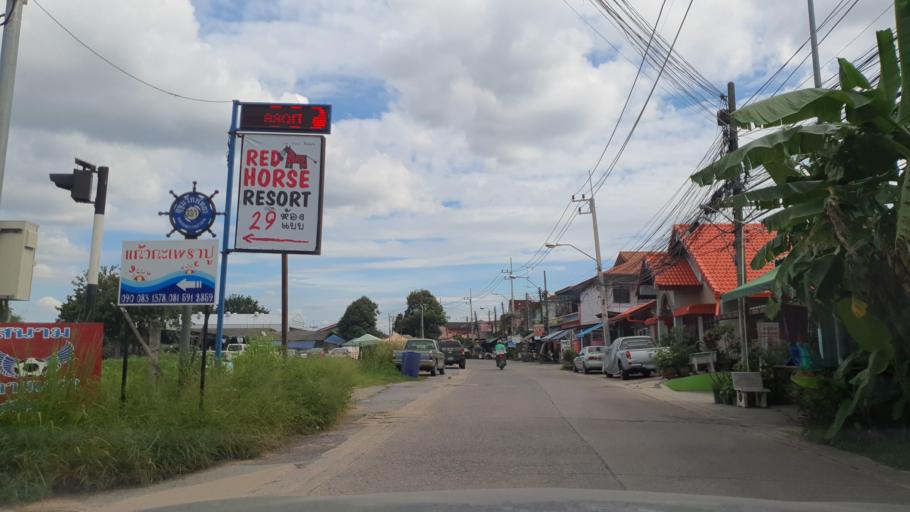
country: TH
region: Chon Buri
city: Phatthaya
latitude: 12.9589
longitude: 100.9097
